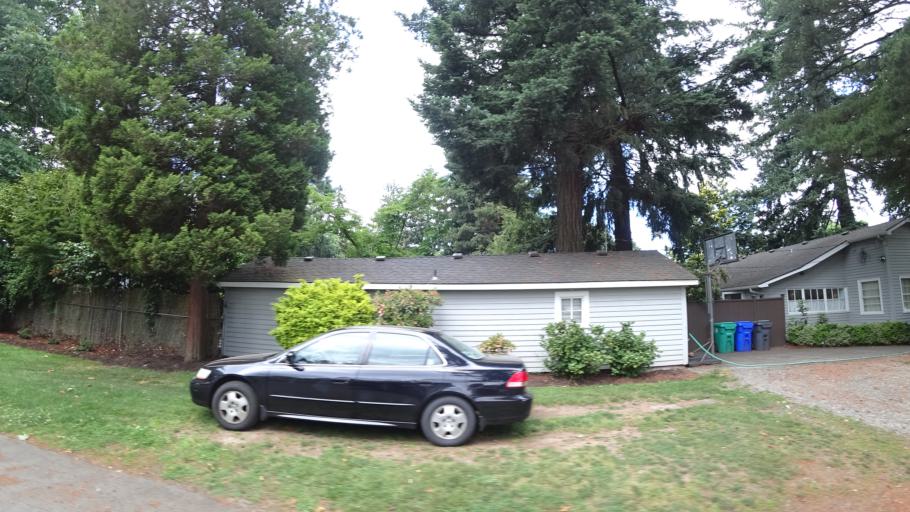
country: US
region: Oregon
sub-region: Multnomah County
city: Portland
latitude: 45.5647
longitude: -122.6118
